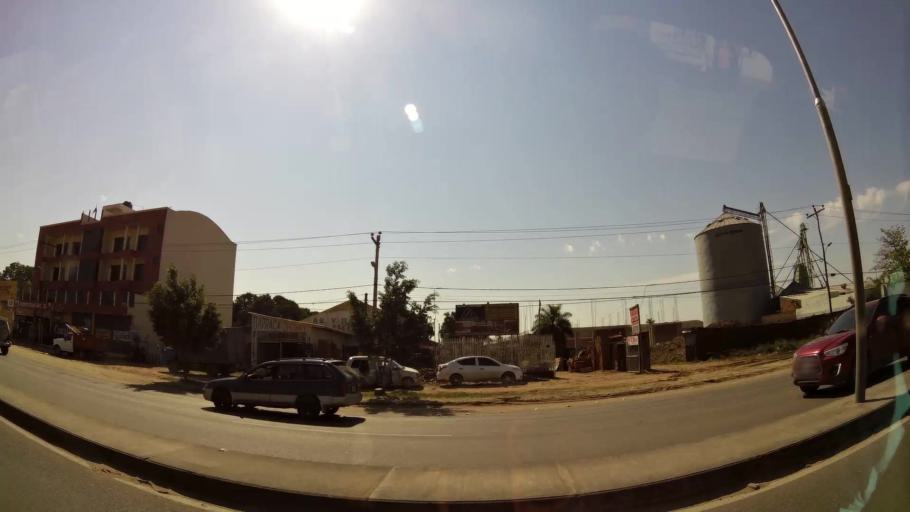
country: BO
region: Santa Cruz
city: Santa Cruz de la Sierra
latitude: -17.7672
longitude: -63.1127
